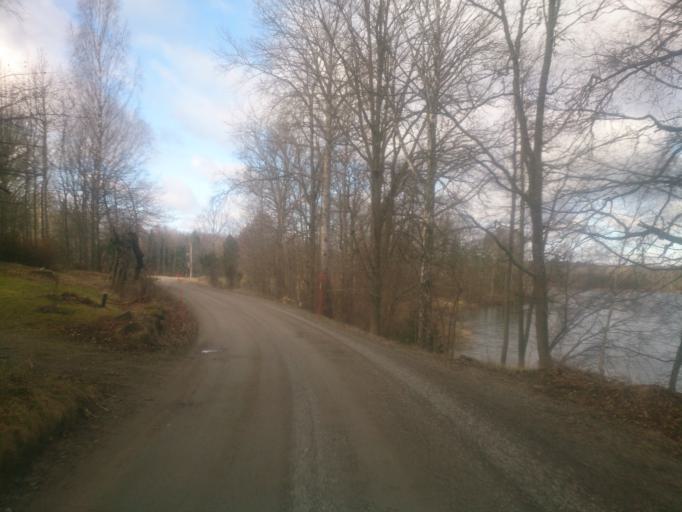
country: SE
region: OEstergoetland
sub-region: Atvidabergs Kommun
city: Atvidaberg
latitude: 58.2052
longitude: 16.1598
